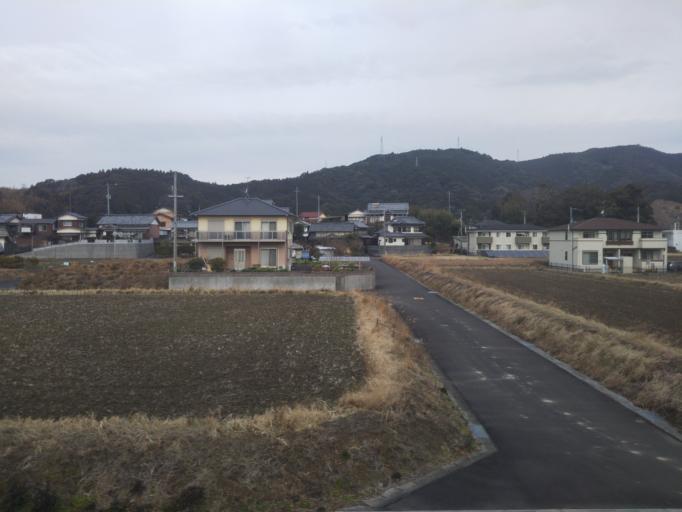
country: JP
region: Kochi
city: Nakamura
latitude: 32.9824
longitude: 132.9572
